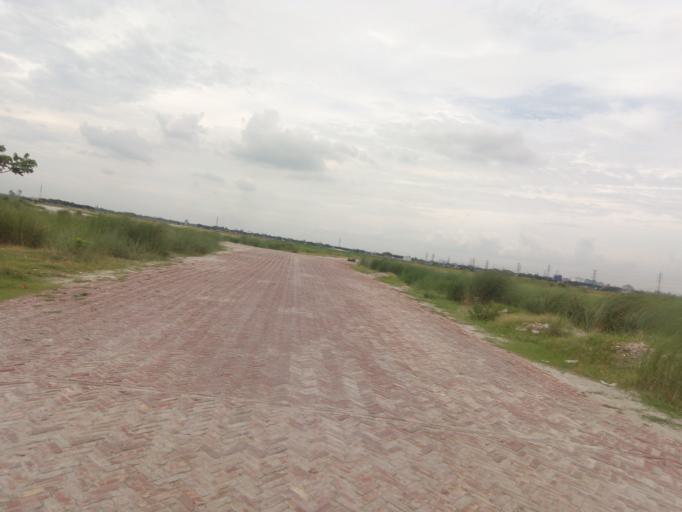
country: BD
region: Dhaka
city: Paltan
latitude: 23.7279
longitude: 90.4545
